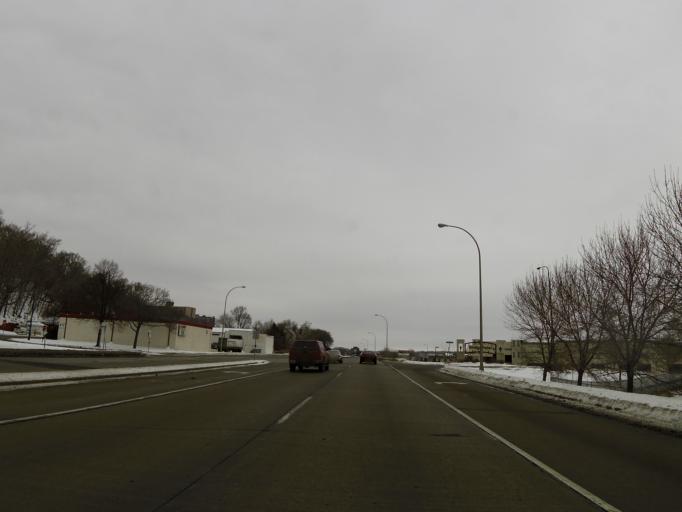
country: US
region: Minnesota
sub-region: Dakota County
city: South Saint Paul
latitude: 44.8867
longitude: -93.0324
